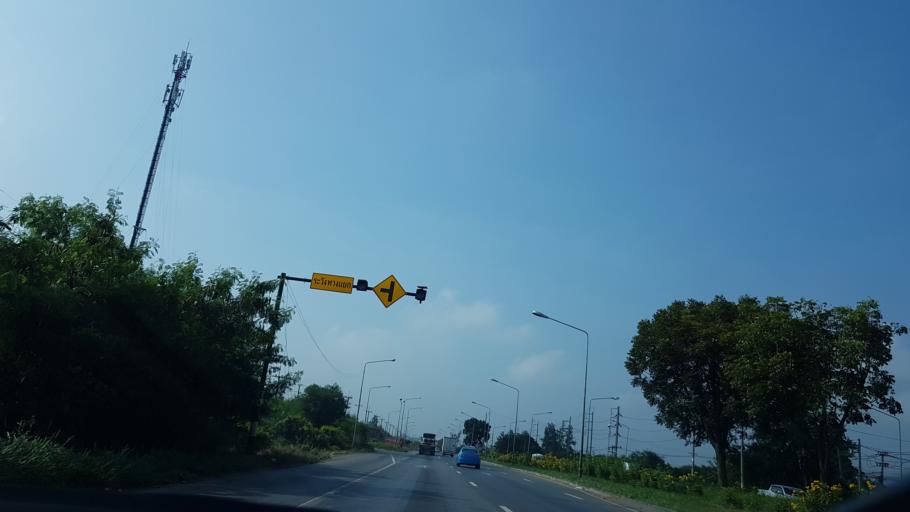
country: TH
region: Pathum Thani
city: Sam Khok
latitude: 14.1309
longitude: 100.5389
